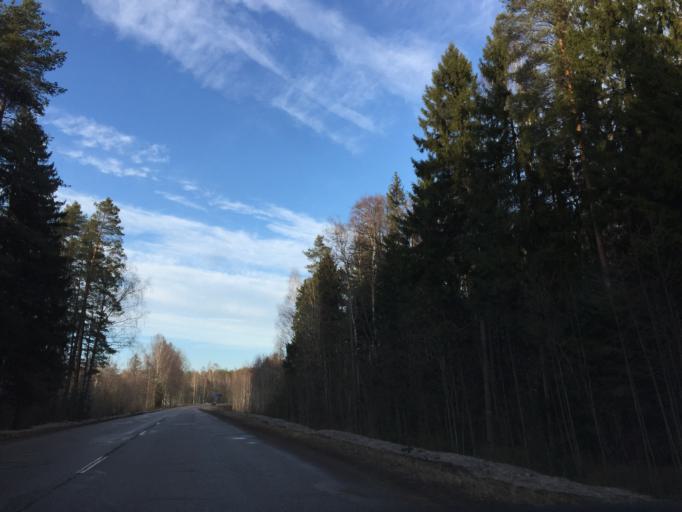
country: LV
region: Kekava
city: Balozi
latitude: 56.7482
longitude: 24.1075
